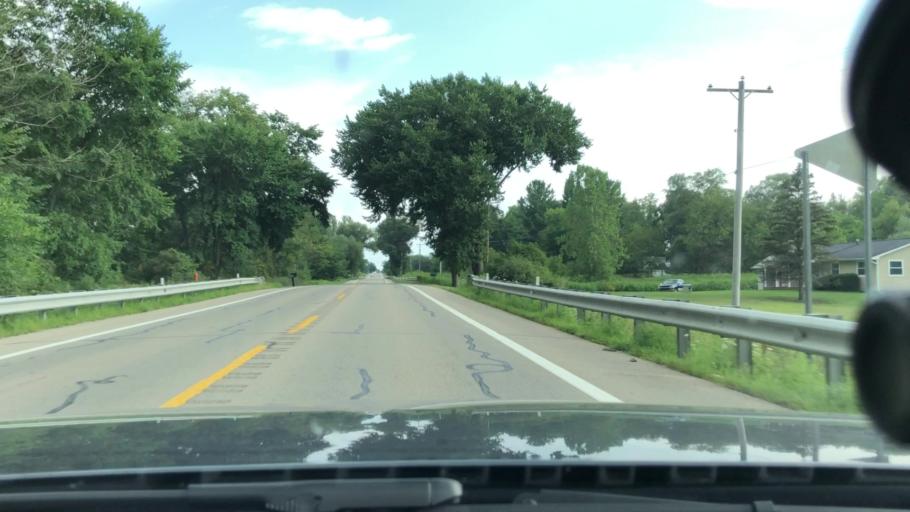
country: US
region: Michigan
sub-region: Washtenaw County
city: Manchester
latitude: 42.2167
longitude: -84.0333
